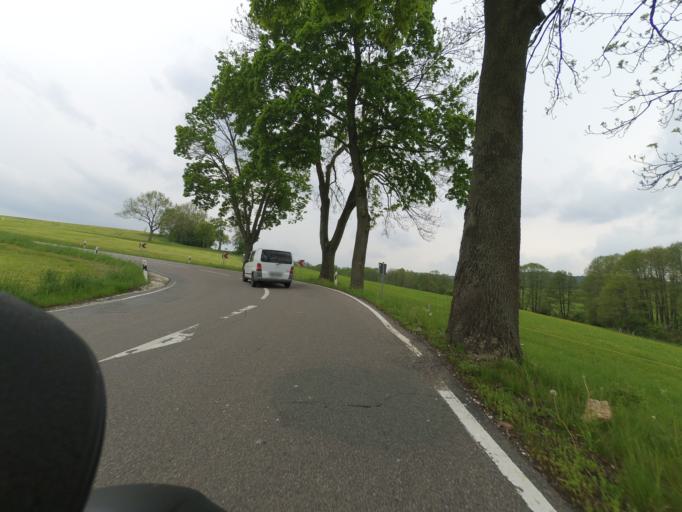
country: DE
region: Saxony
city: Lengefeld
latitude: 50.7349
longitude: 13.1831
